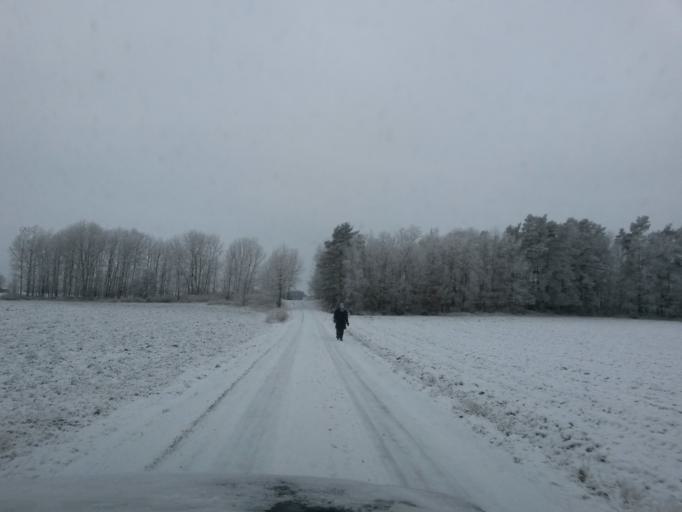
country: SE
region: Vaestra Goetaland
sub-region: Grastorps Kommun
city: Graestorp
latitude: 58.3718
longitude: 12.8326
